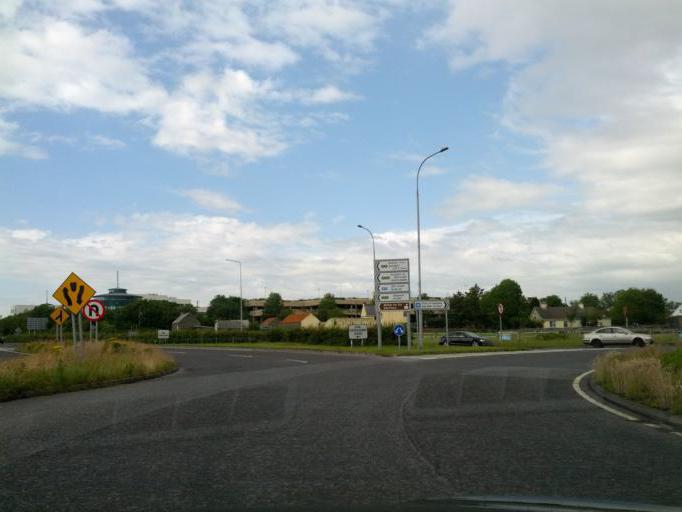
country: IE
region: Connaught
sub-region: County Galway
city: Oranmore
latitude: 53.2792
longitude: -8.9733
